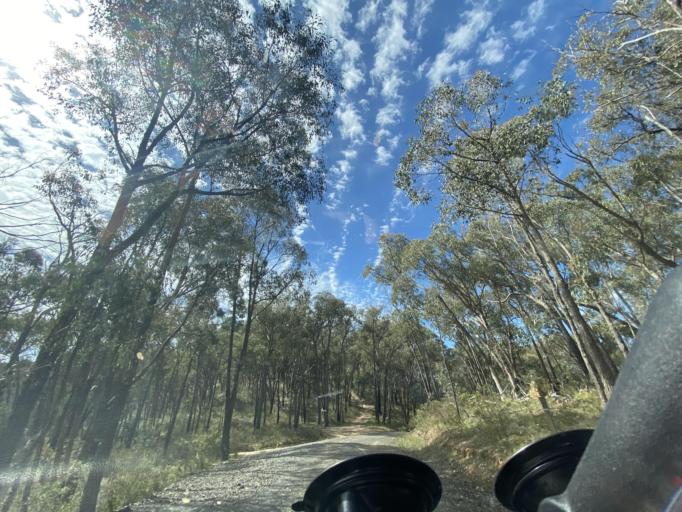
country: AU
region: Victoria
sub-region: Mansfield
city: Mansfield
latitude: -36.8010
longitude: 146.1109
